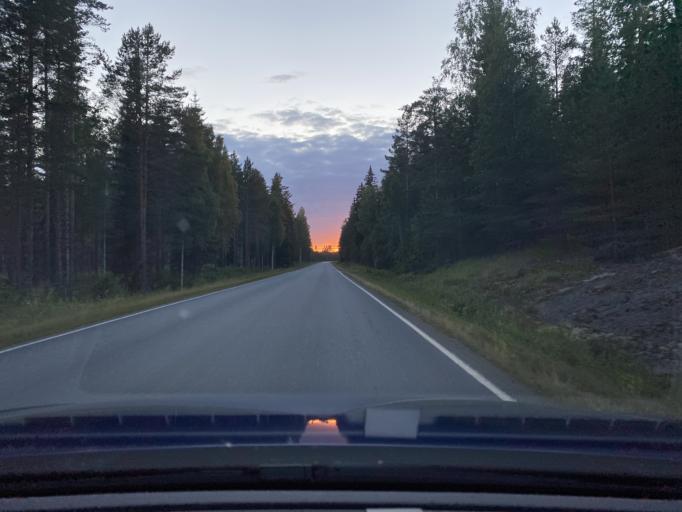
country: FI
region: Haeme
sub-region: Forssa
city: Tammela
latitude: 60.8976
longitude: 23.8916
